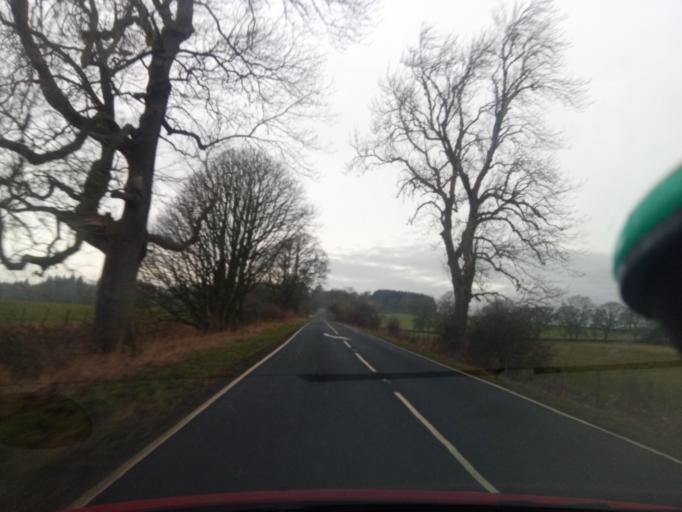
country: GB
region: England
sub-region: Northumberland
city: Wall
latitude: 55.0314
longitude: -2.1643
